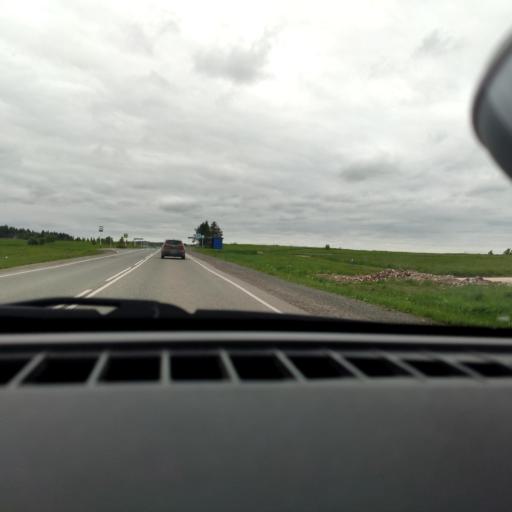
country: RU
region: Perm
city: Ust'-Kachka
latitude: 57.9049
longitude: 55.7790
